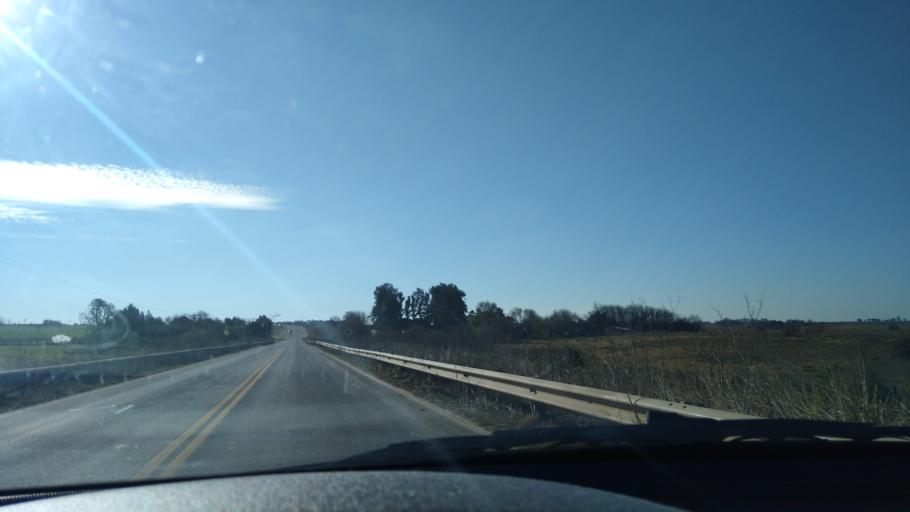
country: AR
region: Entre Rios
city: Aranguren
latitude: -32.4058
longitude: -60.3240
